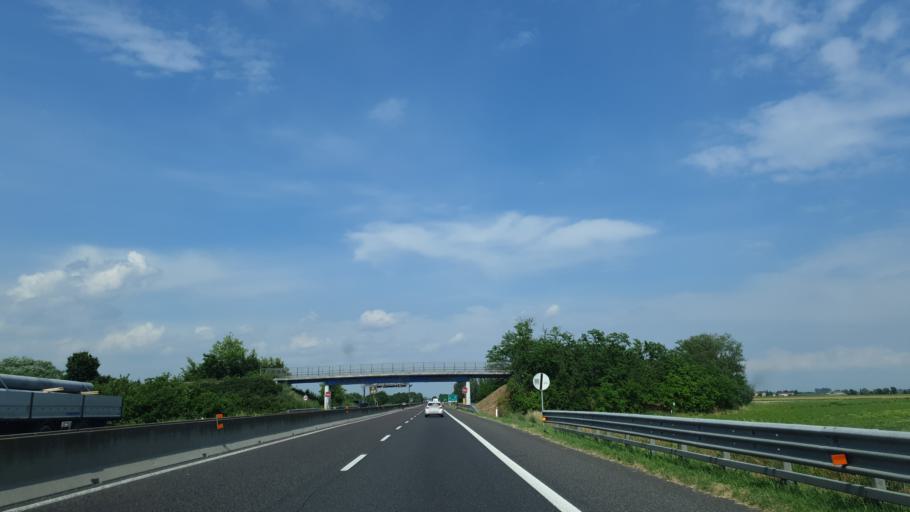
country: IT
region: Veneto
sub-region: Provincia di Rovigo
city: Occhiobello
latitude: 44.9298
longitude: 11.6033
